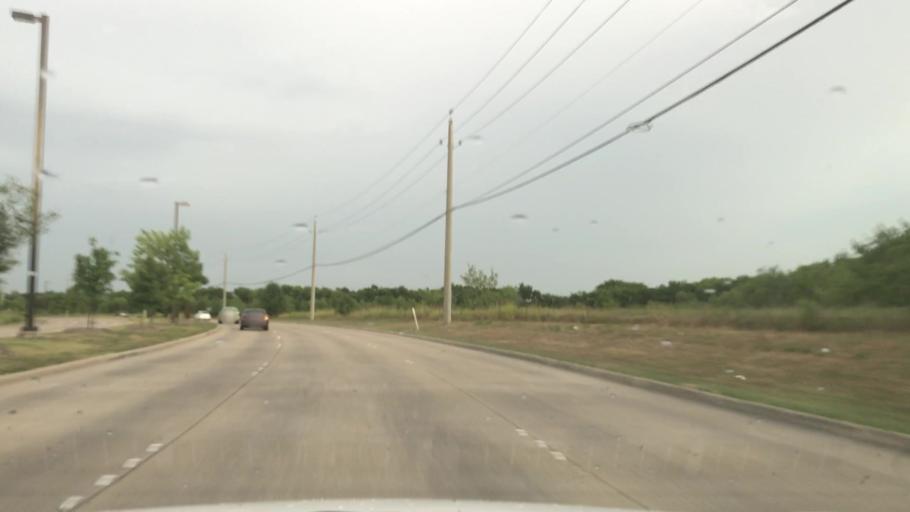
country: US
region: Texas
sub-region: Dallas County
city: Mesquite
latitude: 32.7374
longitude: -96.5712
